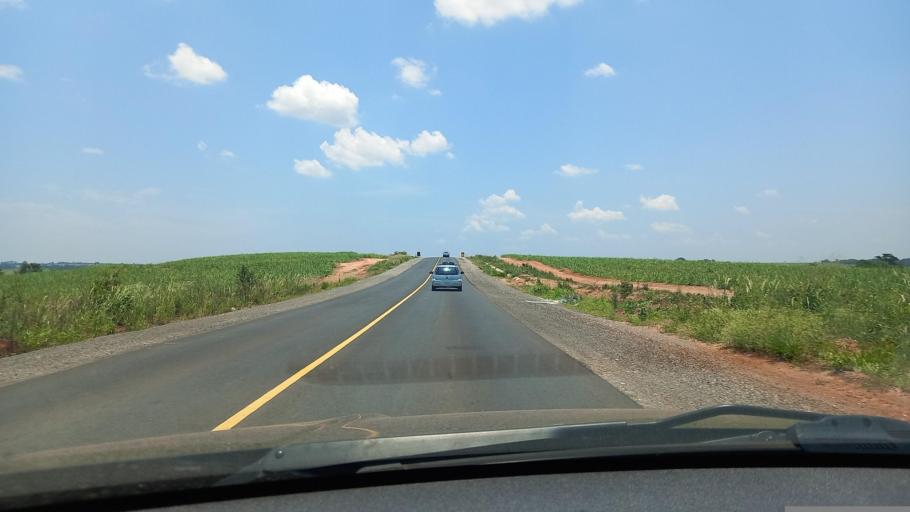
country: BR
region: Sao Paulo
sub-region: Moji-Guacu
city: Mogi-Gaucu
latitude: -22.3689
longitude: -46.8740
